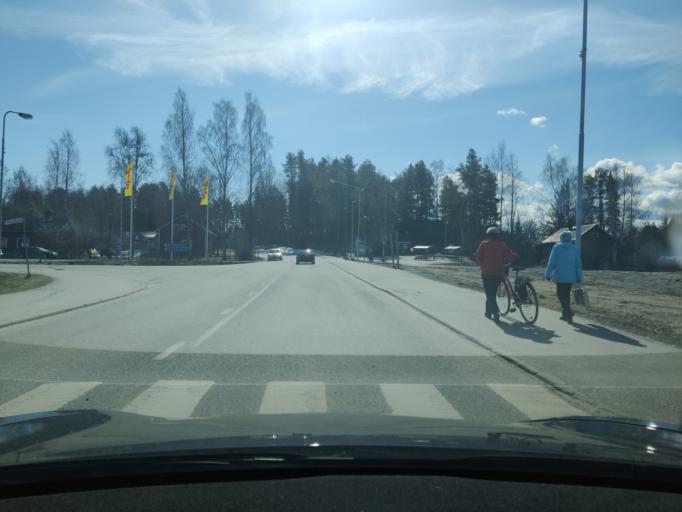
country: FI
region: Northern Savo
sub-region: Kuopio
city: Vehmersalmi
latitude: 62.7613
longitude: 28.0285
